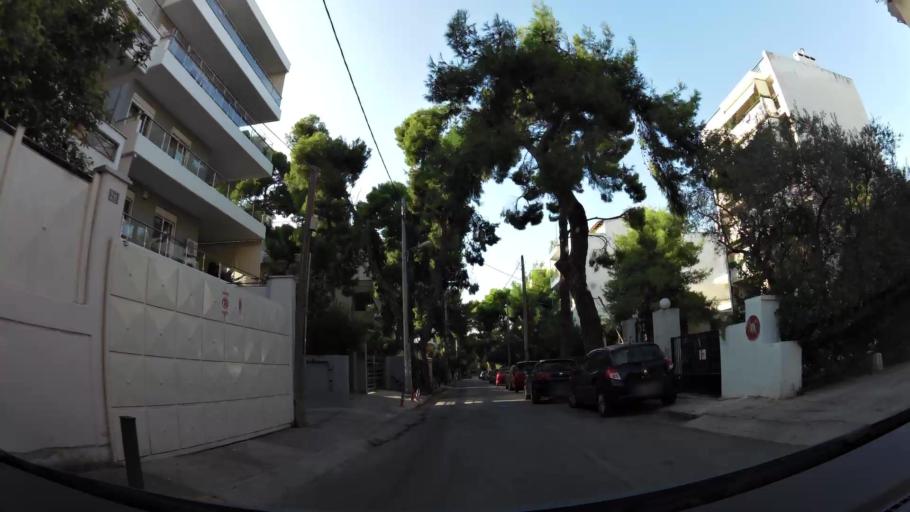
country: GR
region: Attica
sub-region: Nomarchia Athinas
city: Agia Paraskevi
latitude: 38.0088
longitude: 23.8286
